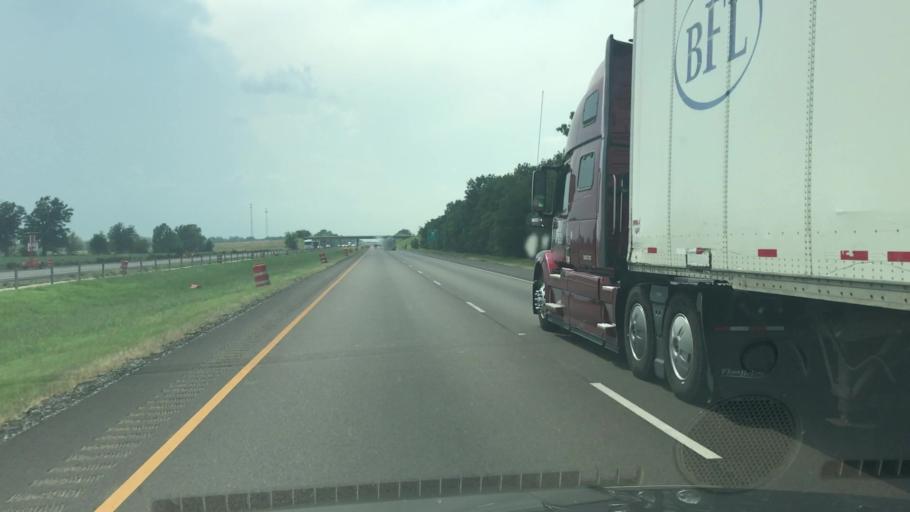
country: US
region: Arkansas
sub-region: Crittenden County
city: Earle
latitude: 35.1336
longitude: -90.4610
